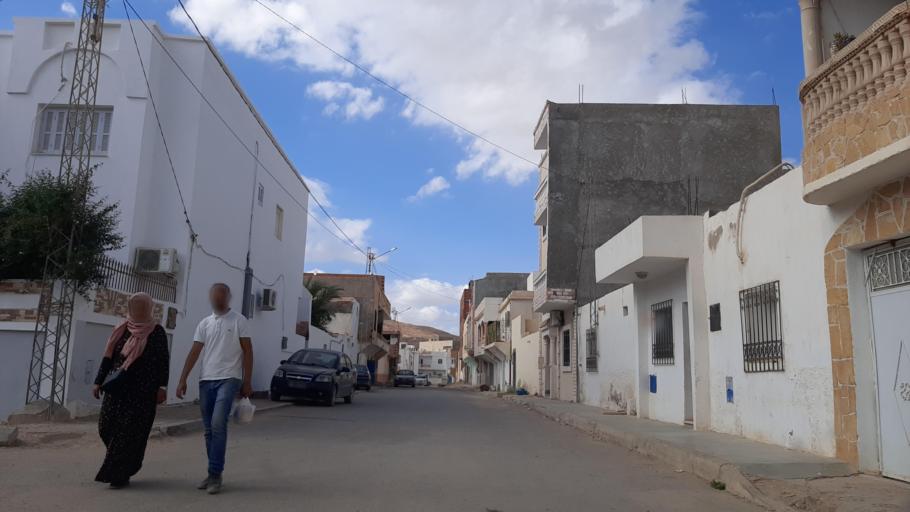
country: TN
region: Tataouine
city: Tataouine
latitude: 32.9304
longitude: 10.4555
